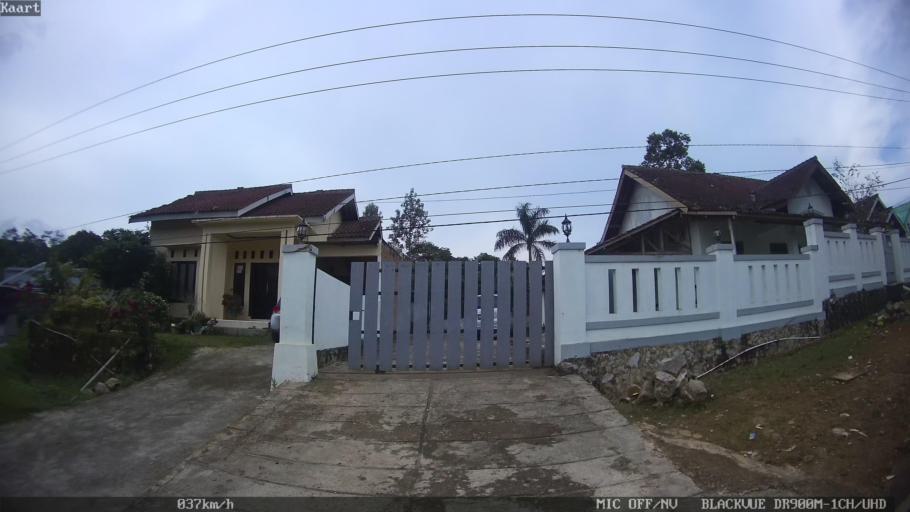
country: ID
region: Lampung
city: Bandarlampung
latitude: -5.4304
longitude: 105.2031
